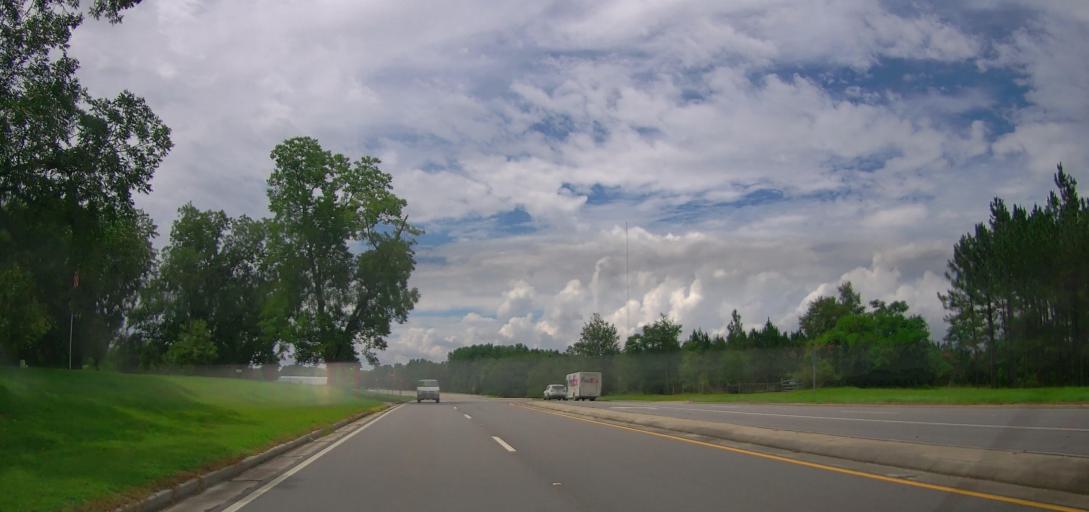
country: US
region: Georgia
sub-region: Telfair County
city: McRae
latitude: 32.0545
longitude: -82.8640
